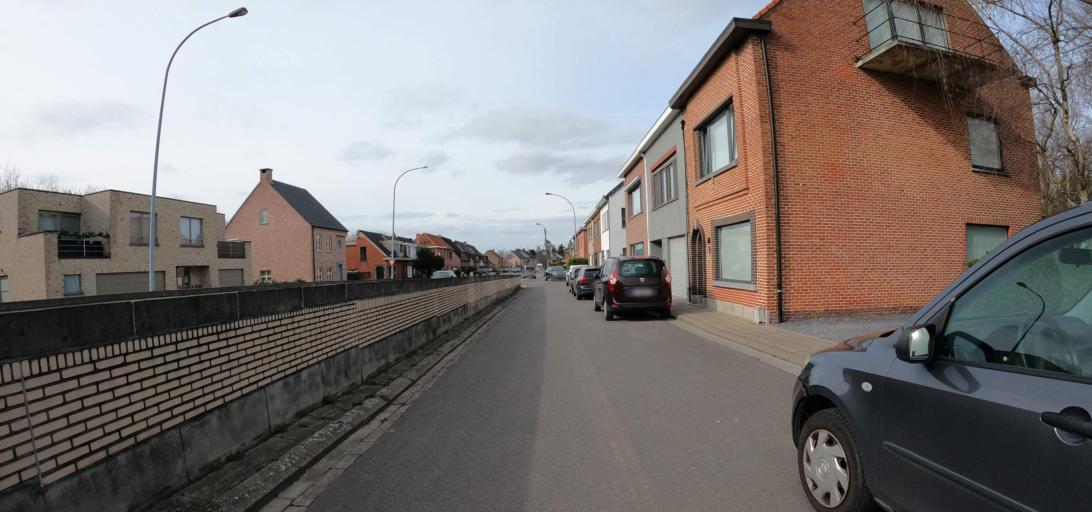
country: BE
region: Flanders
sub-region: Provincie Oost-Vlaanderen
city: Sint-Niklaas
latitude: 51.1783
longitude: 4.1626
